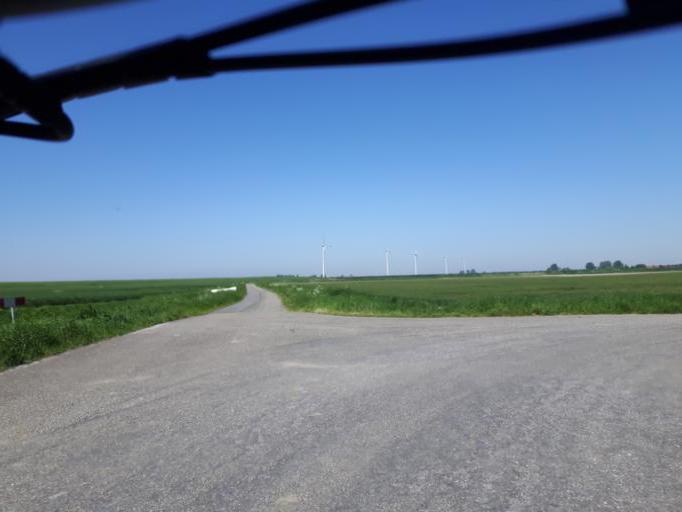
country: NL
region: Zeeland
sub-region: Gemeente Reimerswaal
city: Yerseke
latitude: 51.5483
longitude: 4.0592
